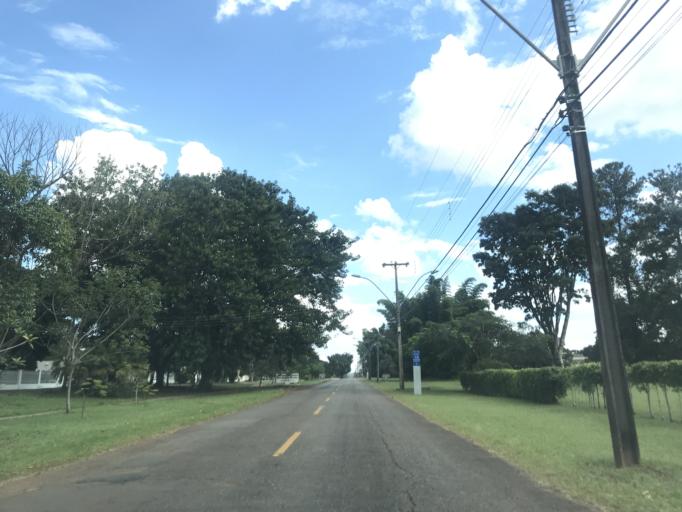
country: BR
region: Federal District
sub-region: Brasilia
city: Brasilia
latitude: -15.9041
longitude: -47.9397
